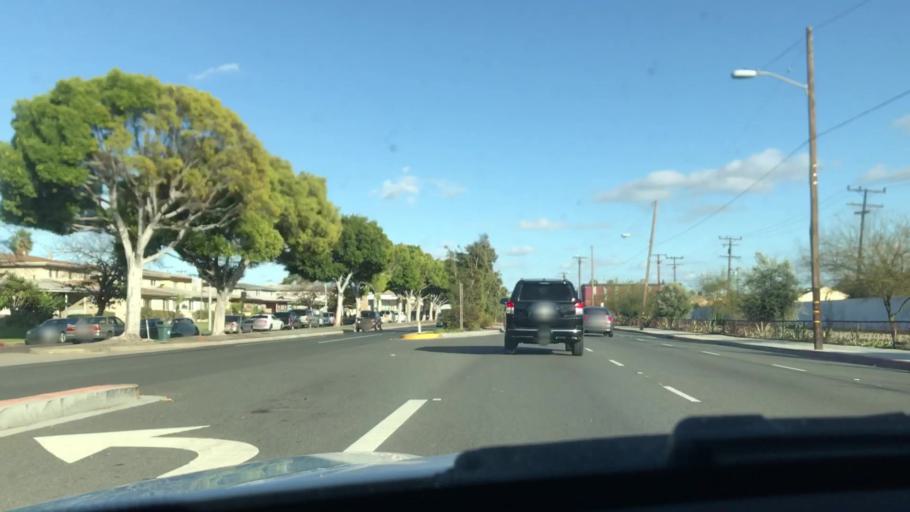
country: US
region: California
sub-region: Los Angeles County
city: Alondra Park
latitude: 33.9019
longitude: -118.3242
